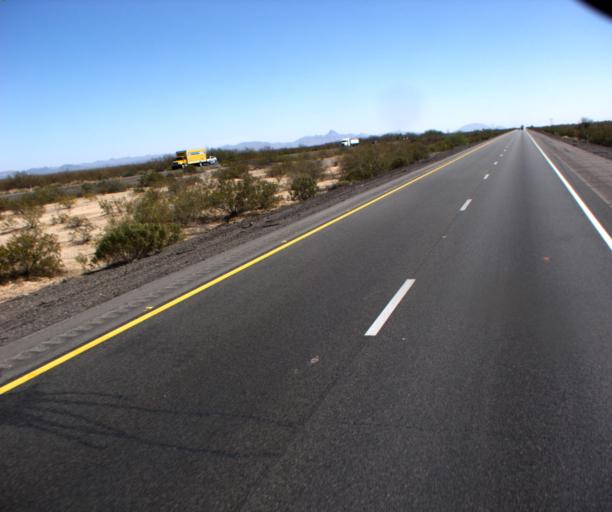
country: US
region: Arizona
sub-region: La Paz County
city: Salome
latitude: 33.5814
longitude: -113.4369
